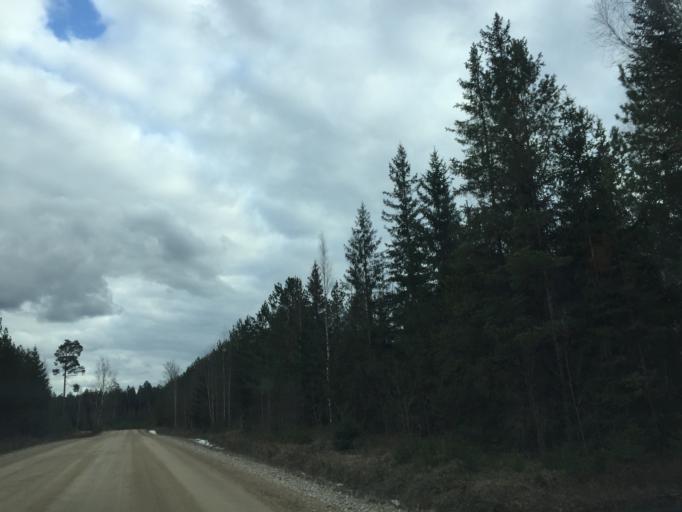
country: LV
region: Ogre
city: Jumprava
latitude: 56.5885
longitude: 24.9931
